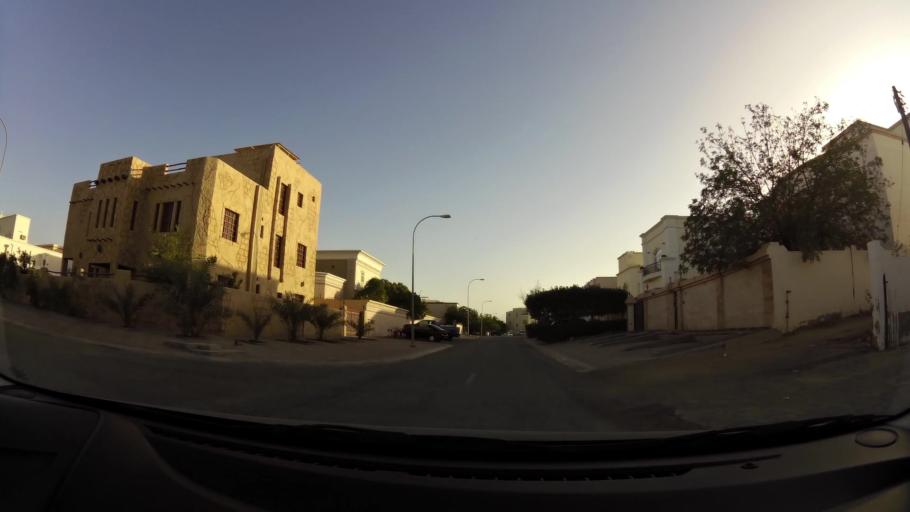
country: OM
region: Muhafazat Masqat
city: As Sib al Jadidah
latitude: 23.6055
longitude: 58.2203
